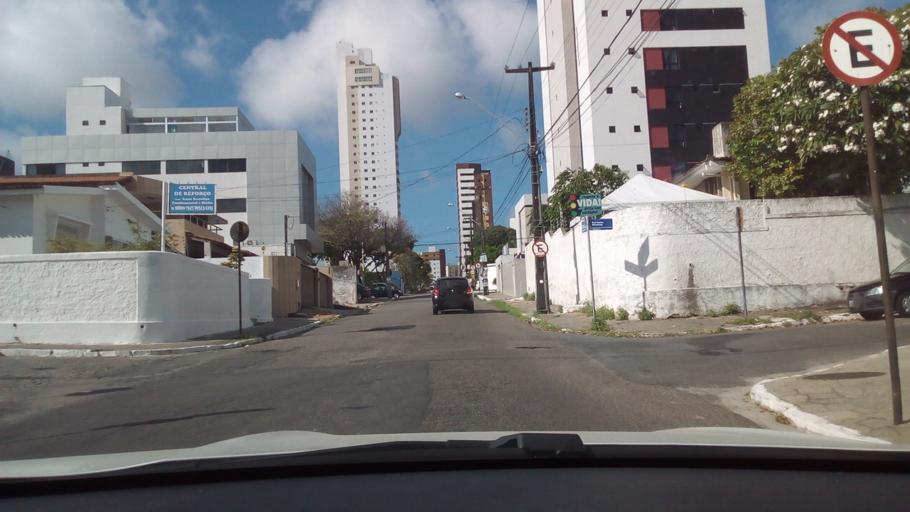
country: BR
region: Paraiba
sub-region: Joao Pessoa
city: Joao Pessoa
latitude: -7.1237
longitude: -34.8411
